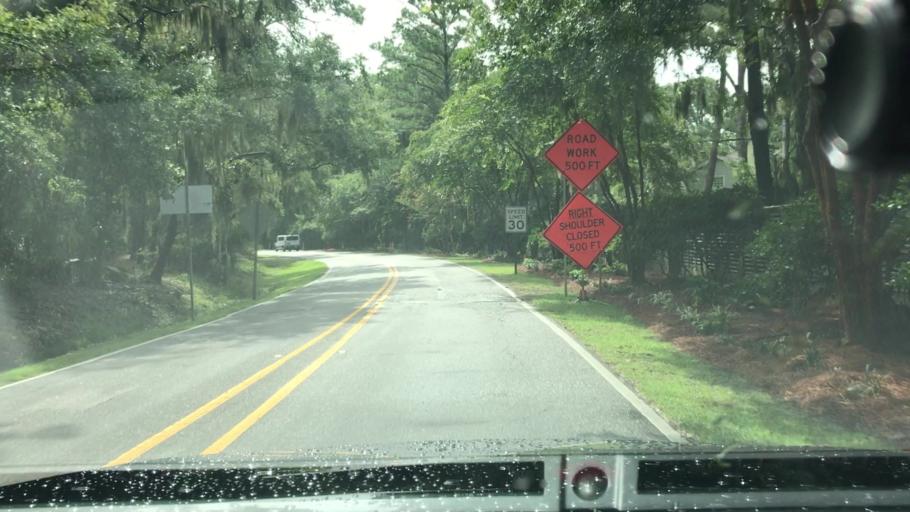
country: US
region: South Carolina
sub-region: Beaufort County
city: Hilton Head Island
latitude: 32.1345
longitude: -80.7728
